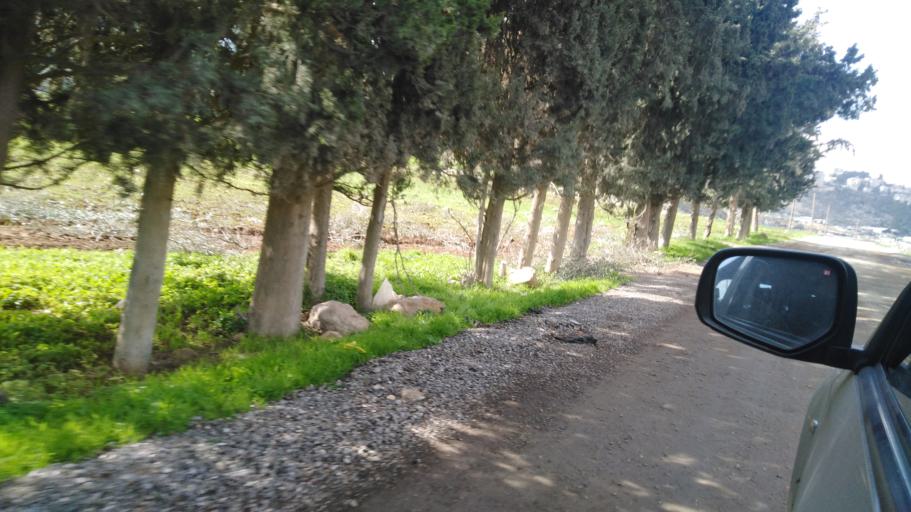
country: PS
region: West Bank
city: Idhna
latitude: 31.5560
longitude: 34.9931
